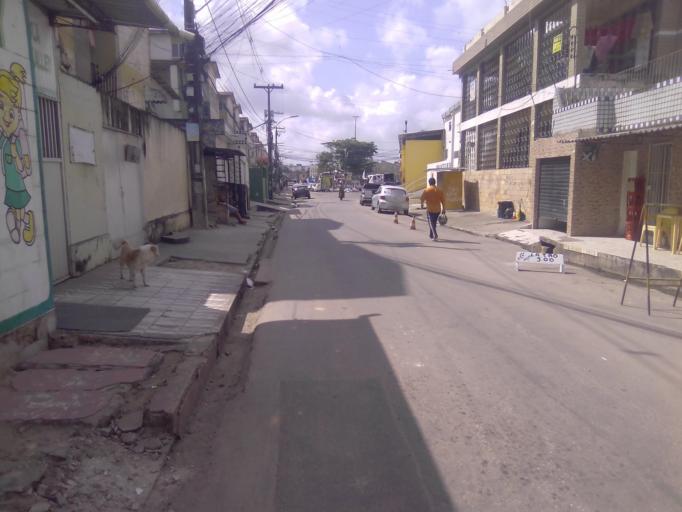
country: BR
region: Pernambuco
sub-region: Jaboatao Dos Guararapes
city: Jaboatao dos Guararapes
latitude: -8.0668
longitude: -34.9967
